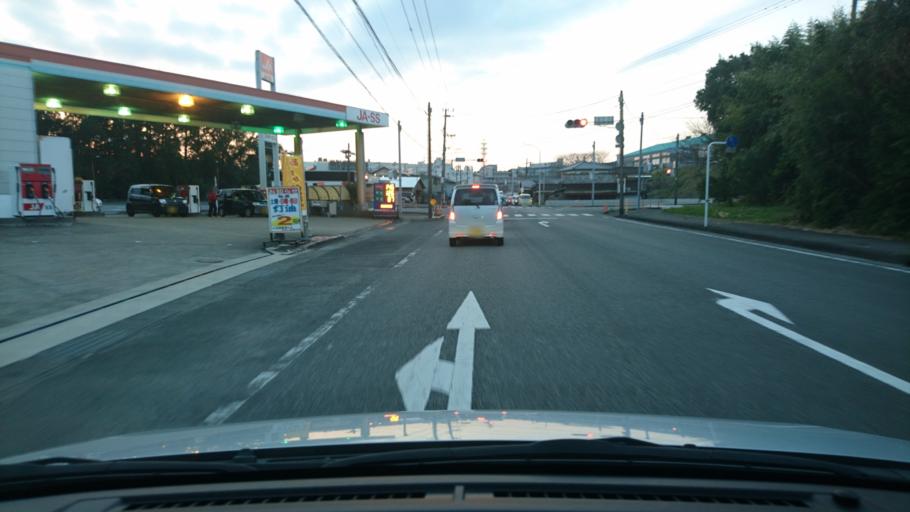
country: JP
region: Miyazaki
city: Miyazaki-shi
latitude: 31.8546
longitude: 131.4098
